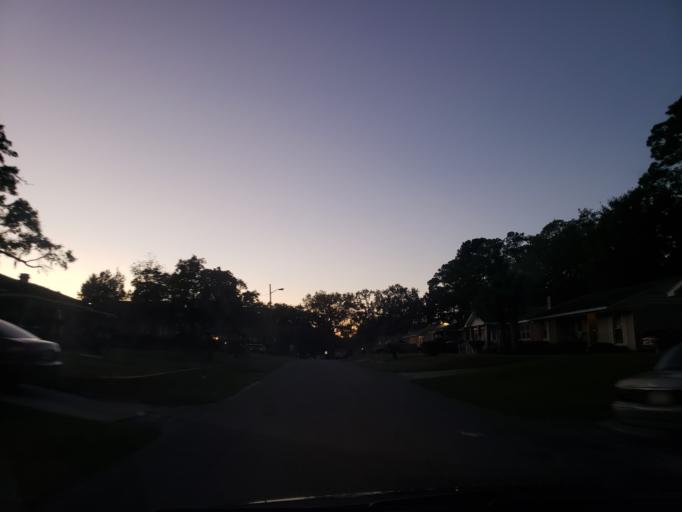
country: US
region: Georgia
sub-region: Chatham County
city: Thunderbolt
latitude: 32.0489
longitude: -81.0760
